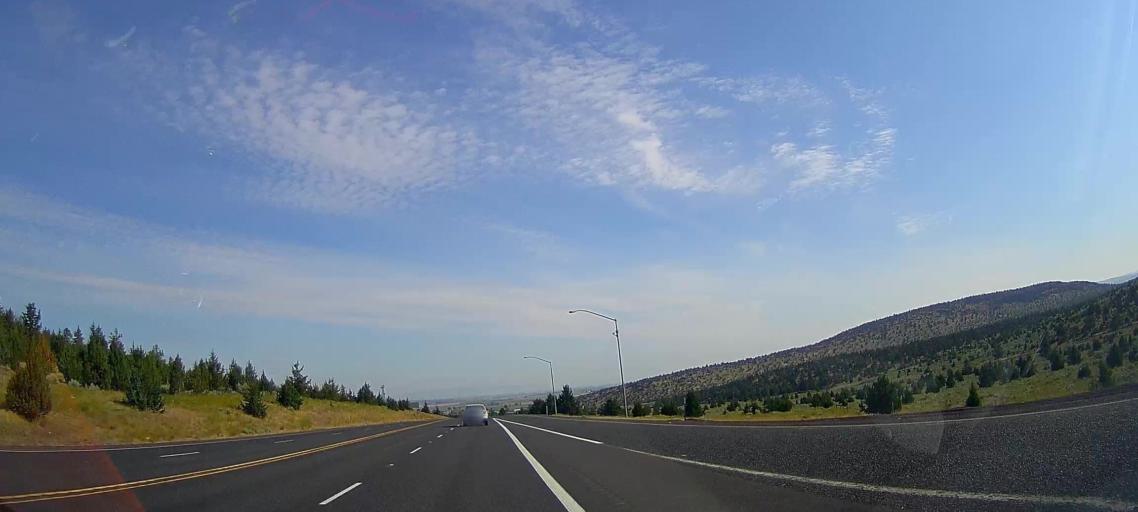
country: US
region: Oregon
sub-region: Jefferson County
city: Culver
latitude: 44.4787
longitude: -121.1938
